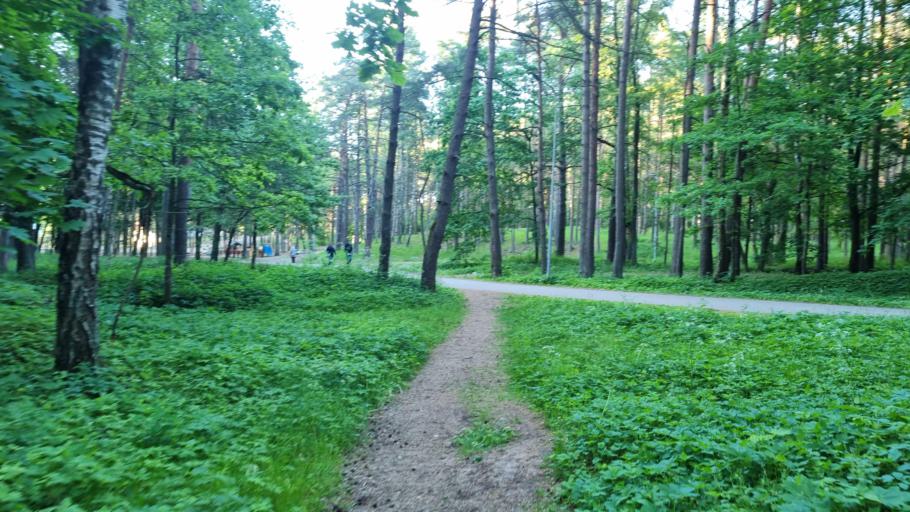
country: LV
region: Marupe
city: Marupe
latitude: 56.9557
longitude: 24.0139
